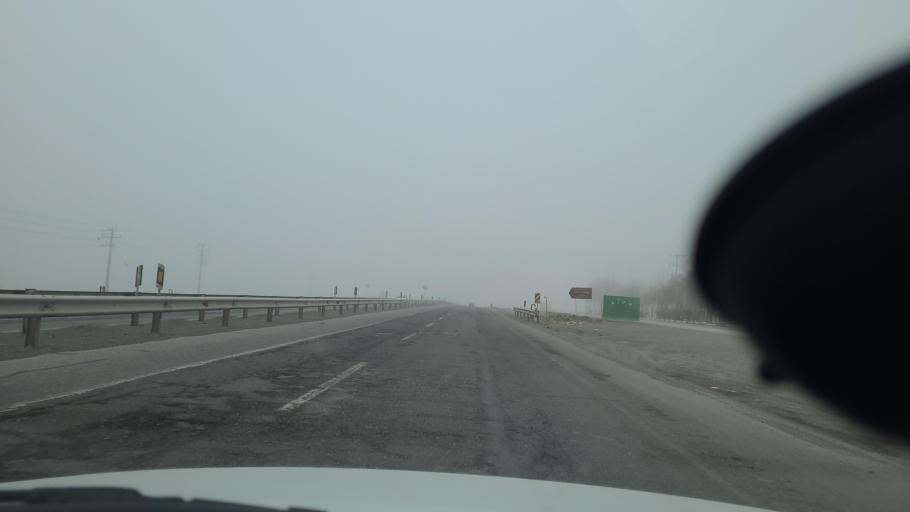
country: IR
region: Razavi Khorasan
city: Fariman
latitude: 35.7679
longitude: 59.7437
